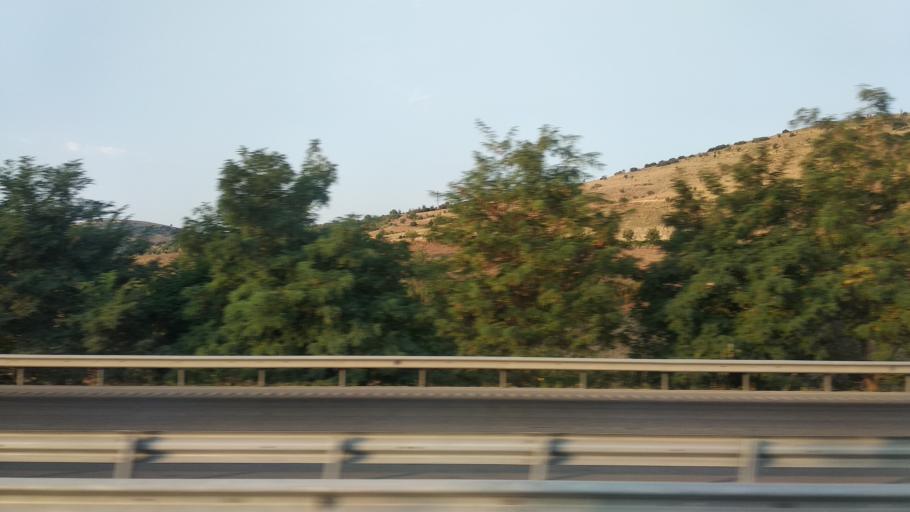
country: TR
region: Manisa
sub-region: Kula
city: Kula
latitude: 38.5658
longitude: 28.5849
